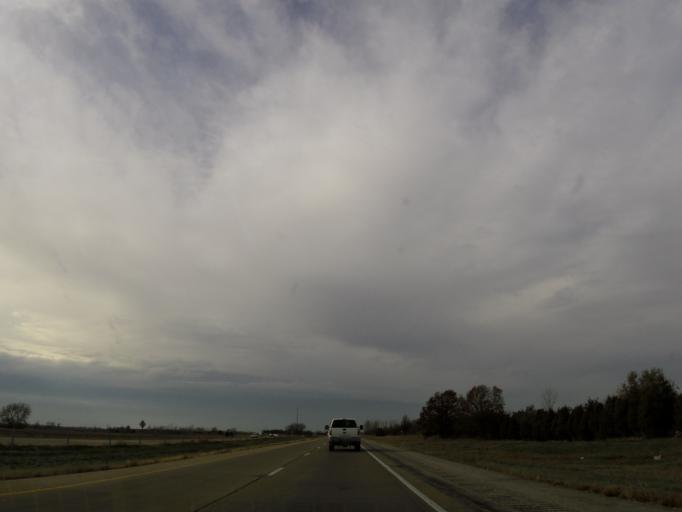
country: US
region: Iowa
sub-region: Scott County
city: Eldridge
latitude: 41.6035
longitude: -90.6630
